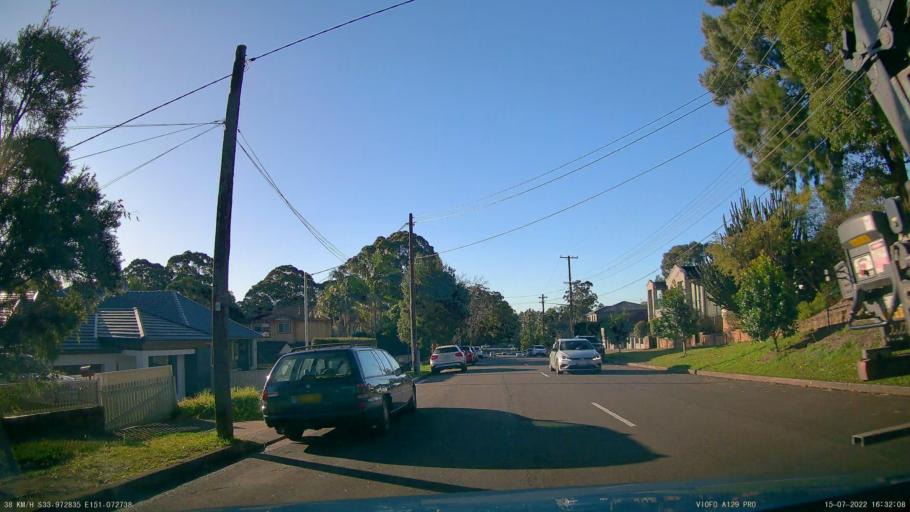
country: AU
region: New South Wales
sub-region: Hurstville
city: Oatley
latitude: -33.9726
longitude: 151.0728
